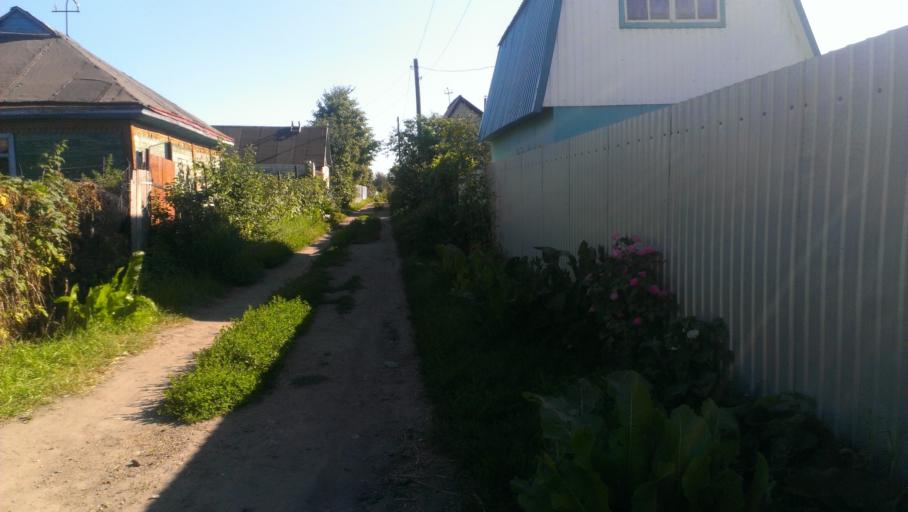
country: RU
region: Altai Krai
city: Novosilikatnyy
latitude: 53.3250
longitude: 83.6698
